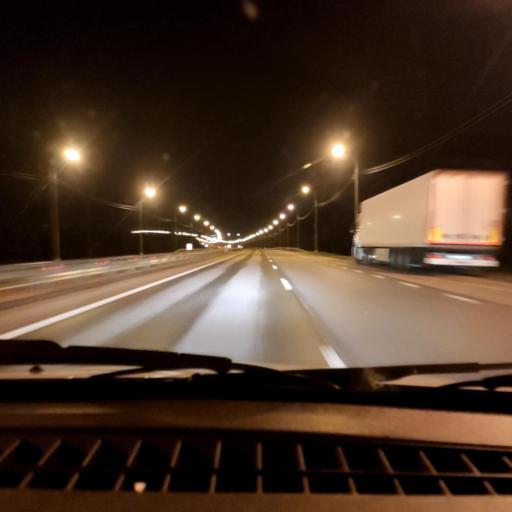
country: RU
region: Lipetsk
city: Khlevnoye
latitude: 52.1315
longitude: 39.1984
